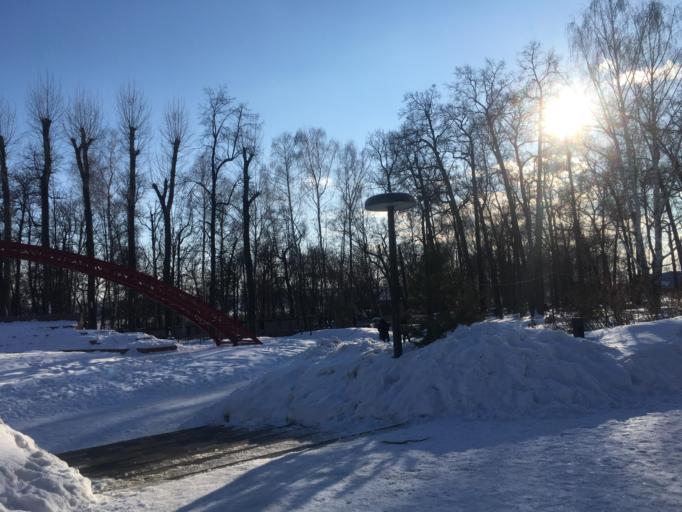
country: RU
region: Tatarstan
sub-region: Zelenodol'skiy Rayon
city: Zelenodolsk
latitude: 55.8457
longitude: 48.4908
